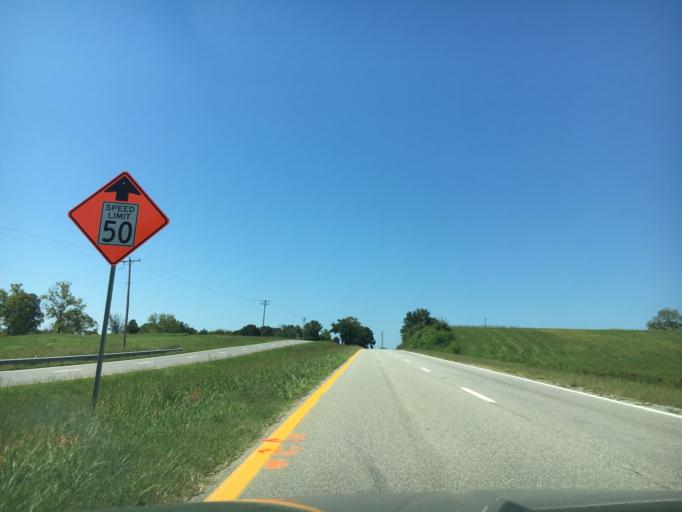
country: US
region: Virginia
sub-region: City of Danville
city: Danville
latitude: 36.5810
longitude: -79.1754
